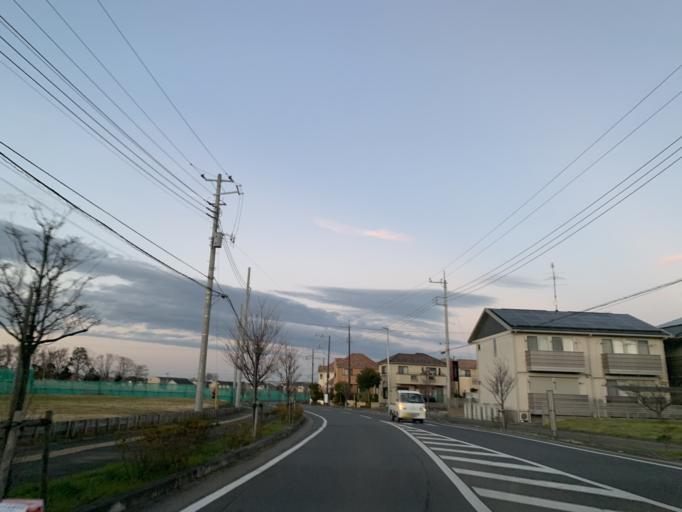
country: JP
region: Ibaraki
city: Moriya
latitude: 35.9120
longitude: 139.9511
